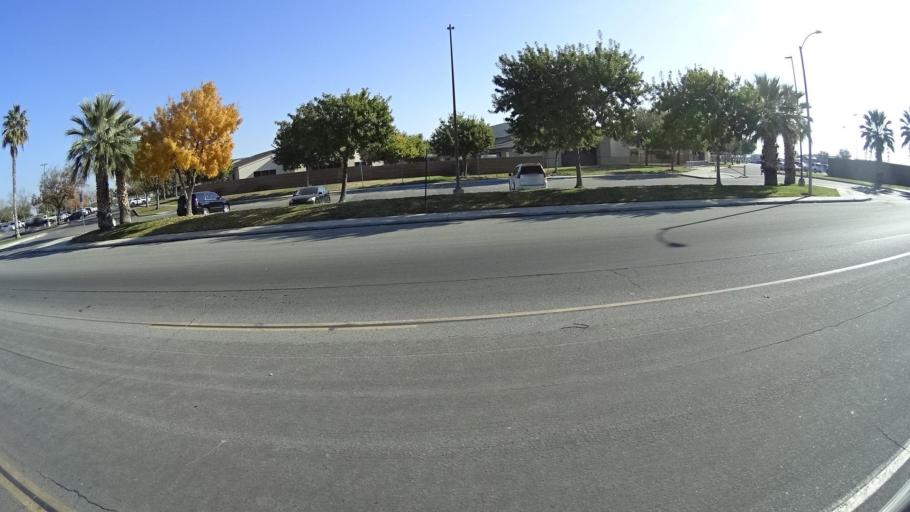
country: US
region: California
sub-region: Kern County
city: Delano
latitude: 35.7674
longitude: -119.2233
